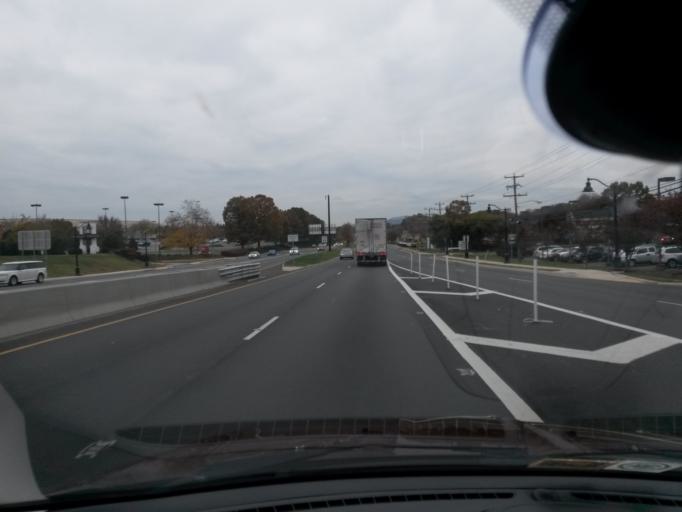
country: US
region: Virginia
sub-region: Albemarle County
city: Hollymead
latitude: 38.0804
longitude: -78.4753
